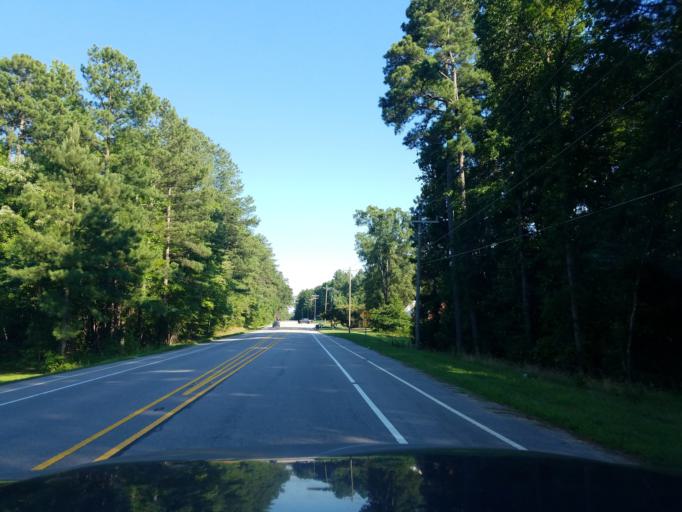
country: US
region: North Carolina
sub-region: Wake County
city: Green Level
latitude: 35.8775
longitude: -78.9518
